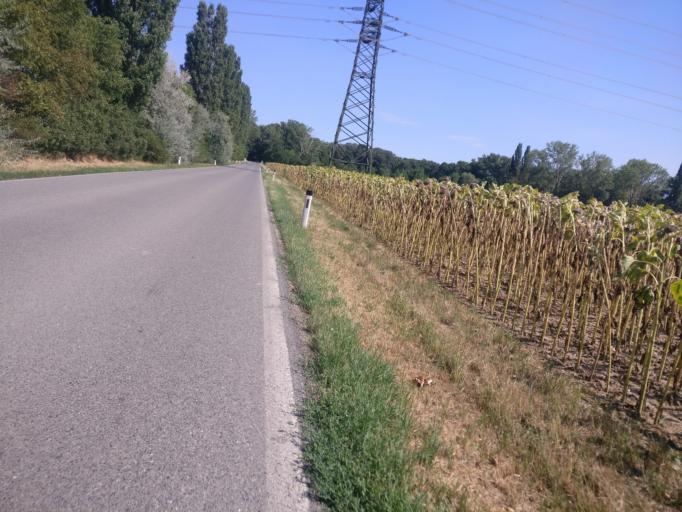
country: AT
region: Lower Austria
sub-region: Politischer Bezirk Modling
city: Guntramsdorf
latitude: 48.0267
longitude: 16.3181
